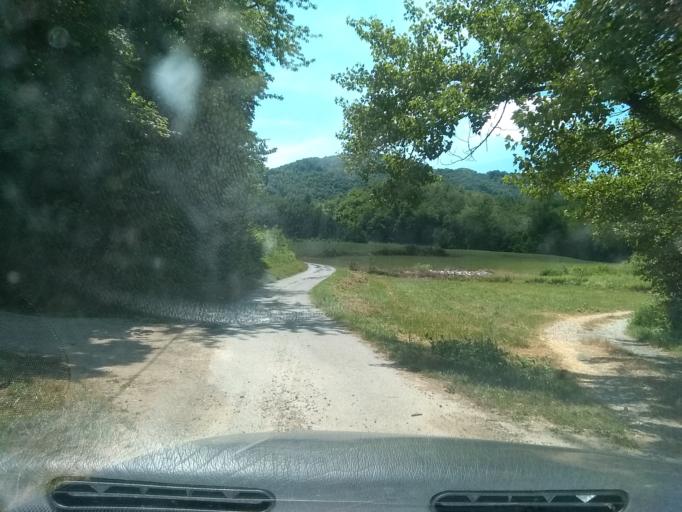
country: SI
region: Bistrica ob Sotli
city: Bistrica ob Sotli
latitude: 46.0670
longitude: 15.7452
